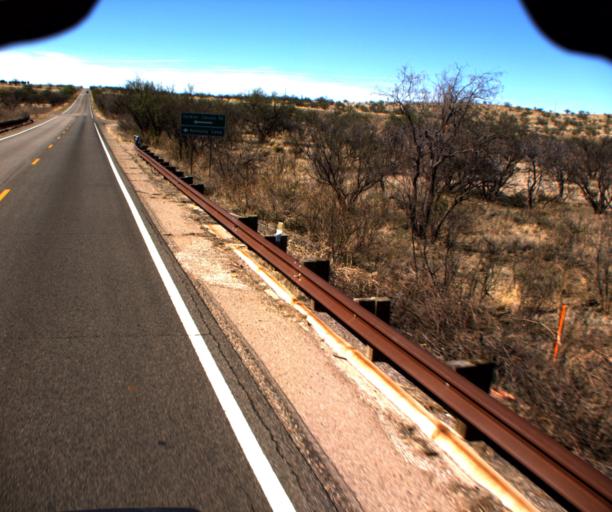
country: US
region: Arizona
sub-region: Pima County
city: Corona de Tucson
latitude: 31.7363
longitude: -110.6626
